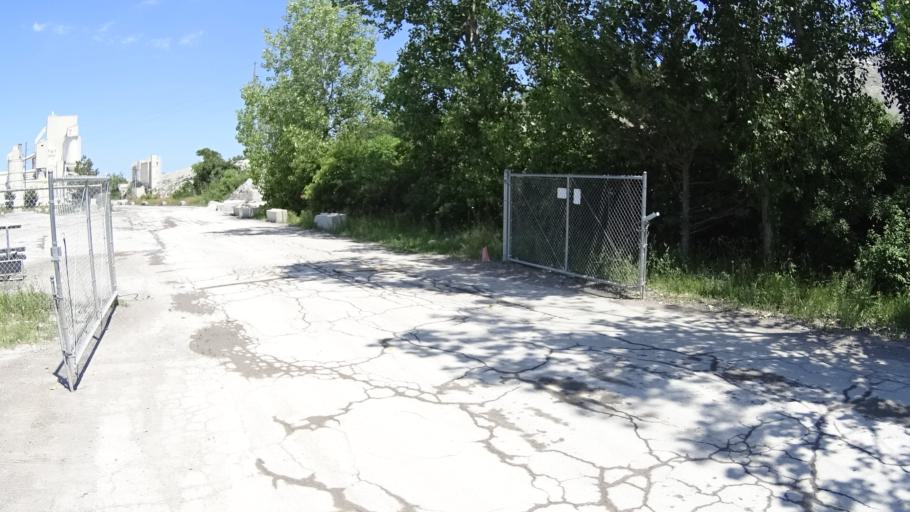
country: US
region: Ohio
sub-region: Erie County
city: Huron
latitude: 41.3937
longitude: -82.5477
